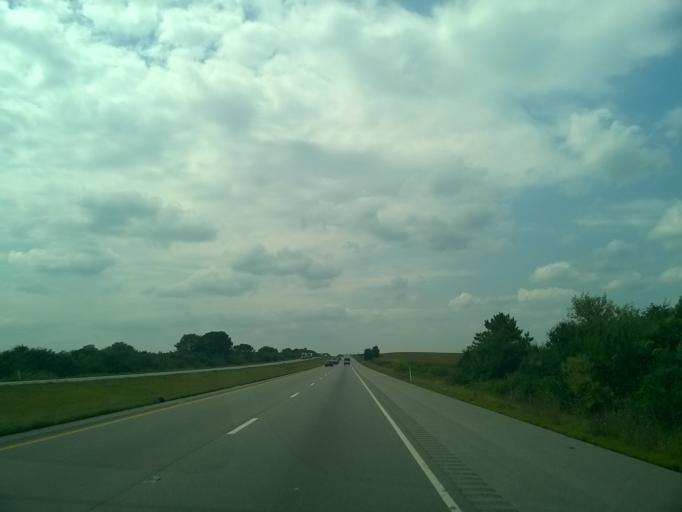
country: US
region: Indiana
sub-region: Putnam County
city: Cloverdale
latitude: 39.5541
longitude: -86.6951
